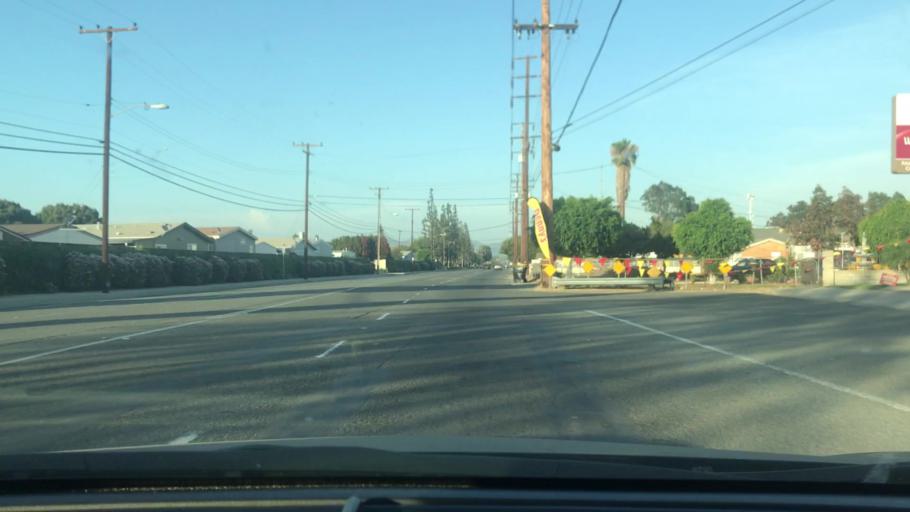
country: US
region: California
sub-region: Orange County
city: Placentia
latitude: 33.8624
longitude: -117.8727
